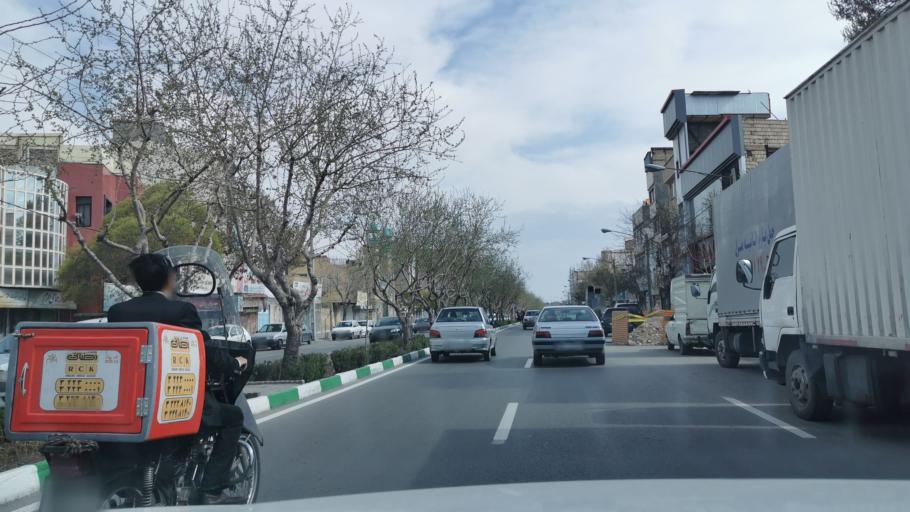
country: IR
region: Razavi Khorasan
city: Mashhad
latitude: 36.3146
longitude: 59.6111
